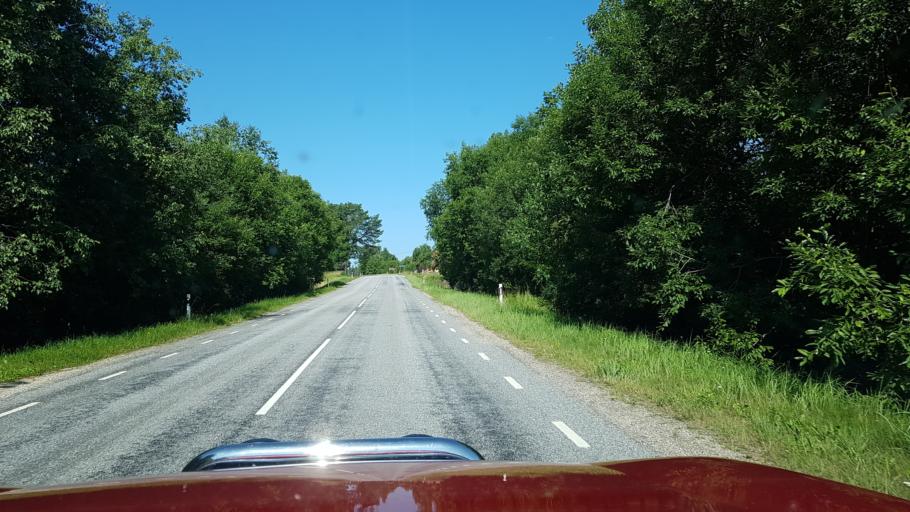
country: EE
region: Polvamaa
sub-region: Polva linn
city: Polva
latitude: 58.0888
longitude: 26.8242
